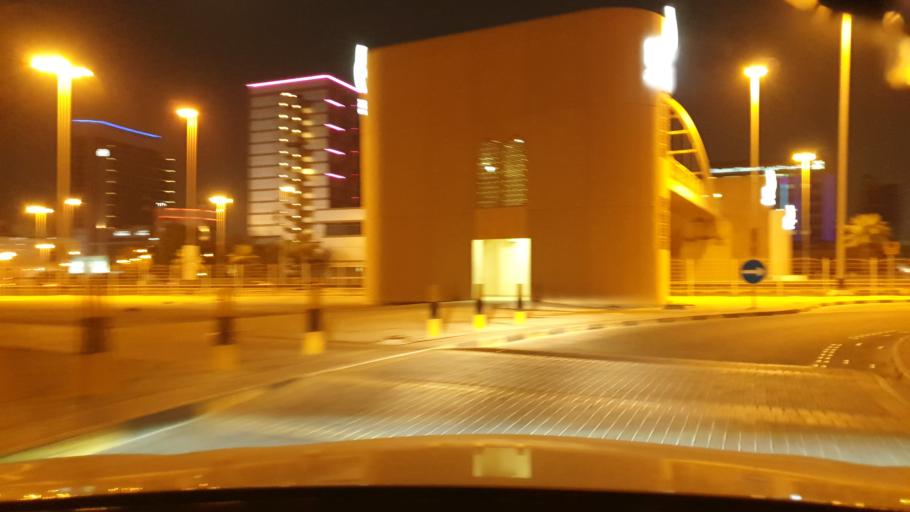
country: BH
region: Manama
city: Manama
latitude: 26.2359
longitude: 50.5721
